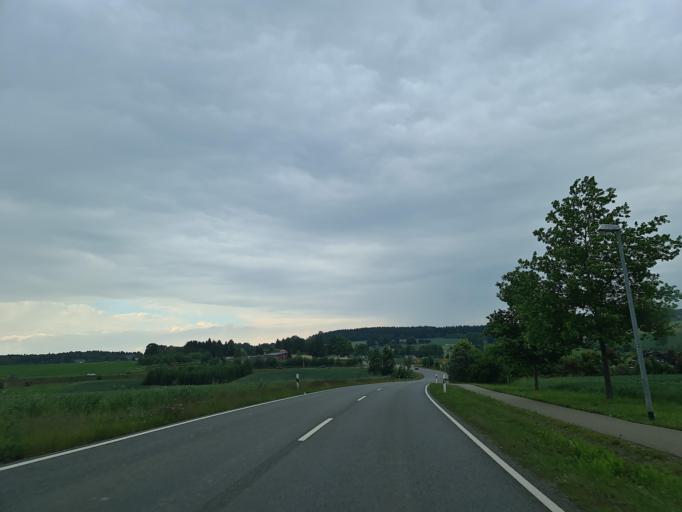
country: DE
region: Saxony
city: Treuen
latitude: 50.5439
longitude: 12.3120
